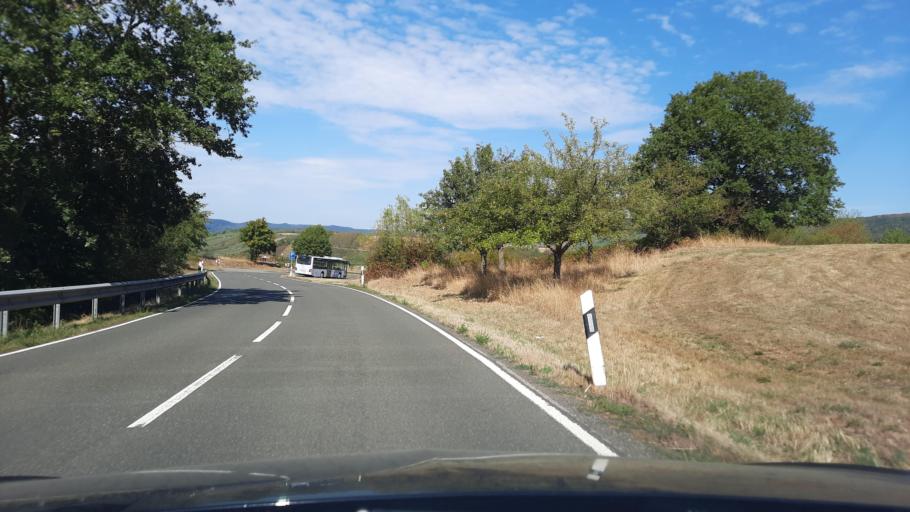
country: DE
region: Rheinland-Pfalz
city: Irsch
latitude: 49.6001
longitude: 6.5935
